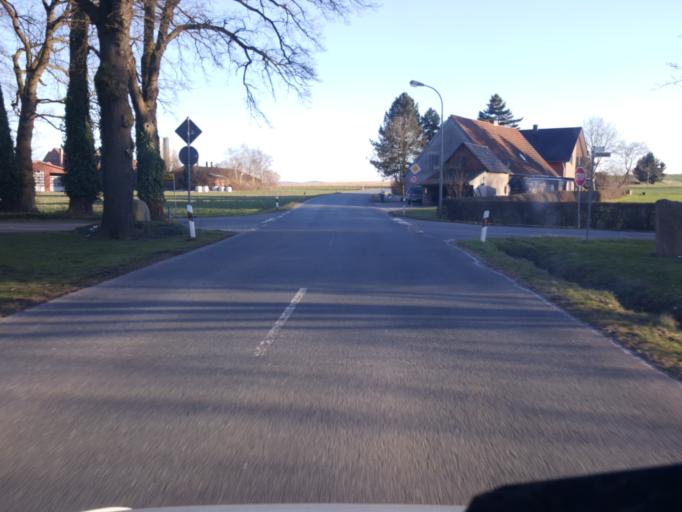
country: DE
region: North Rhine-Westphalia
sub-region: Regierungsbezirk Detmold
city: Hille
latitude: 52.3543
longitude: 8.7314
